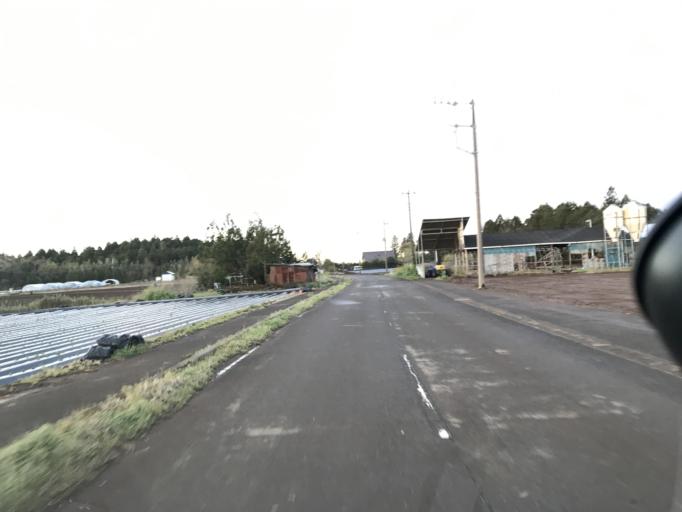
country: JP
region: Chiba
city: Sawara
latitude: 35.8228
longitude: 140.4958
